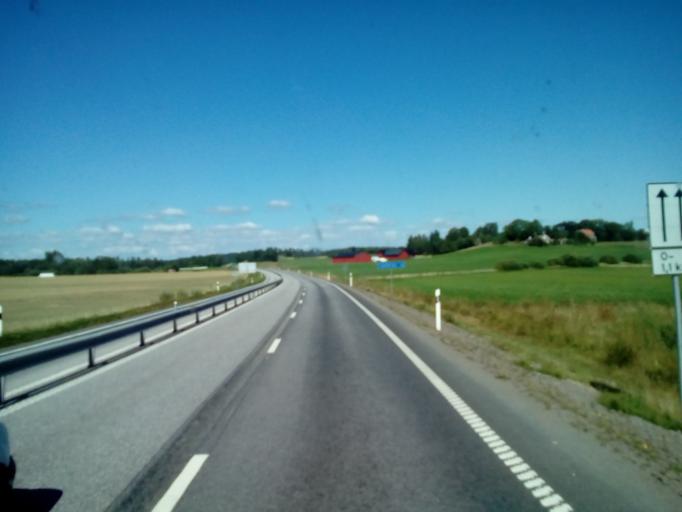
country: SE
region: OEstergoetland
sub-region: Kinda Kommun
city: Rimforsa
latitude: 58.1400
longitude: 15.6809
